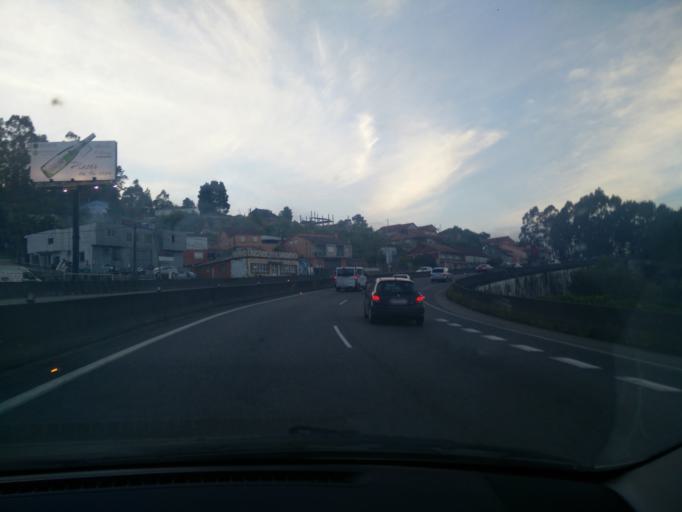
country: ES
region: Galicia
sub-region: Provincia de Pontevedra
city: Porrino
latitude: 42.1941
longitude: -8.6532
